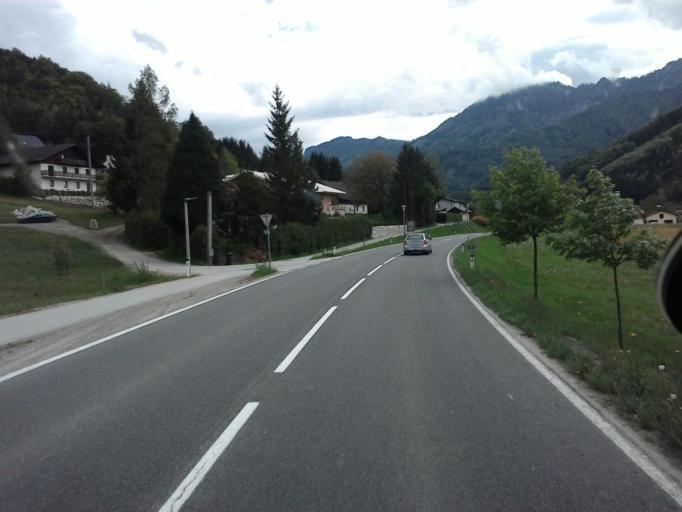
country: AT
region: Upper Austria
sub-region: Politischer Bezirk Kirchdorf an der Krems
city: Micheldorf in Oberoesterreich
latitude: 47.8611
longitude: 14.1522
